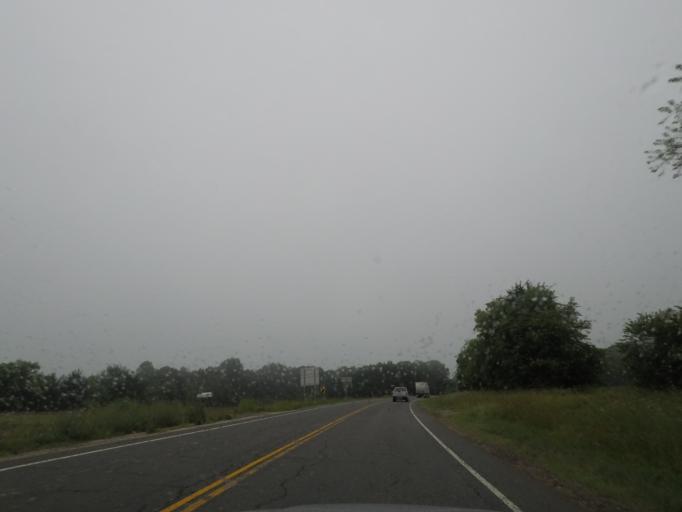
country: US
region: Virginia
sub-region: Buckingham County
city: Buckingham
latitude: 37.5206
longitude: -78.4949
